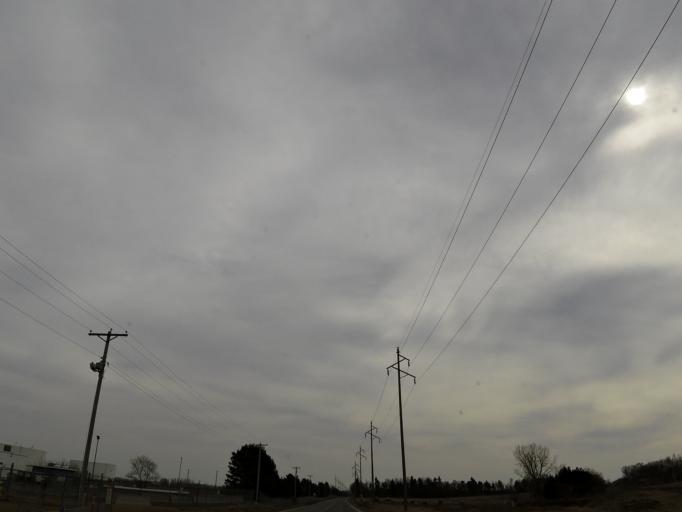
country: US
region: Minnesota
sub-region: Dakota County
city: Rosemount
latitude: 44.7731
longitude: -93.0595
